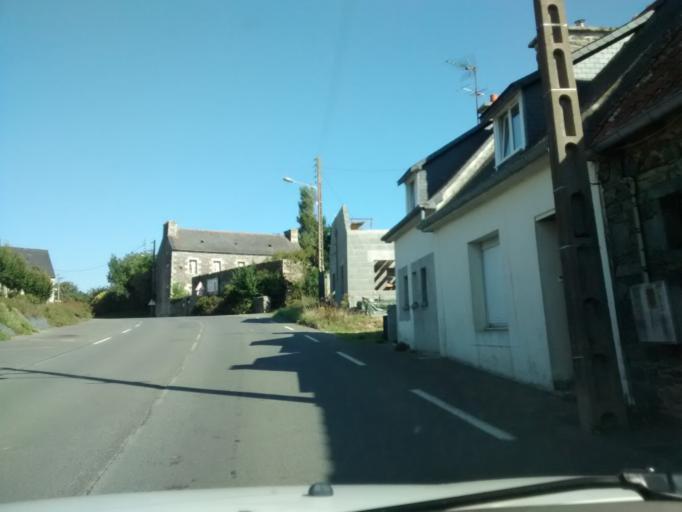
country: FR
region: Brittany
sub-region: Departement des Cotes-d'Armor
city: Tredarzec
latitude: 48.7884
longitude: -3.1988
